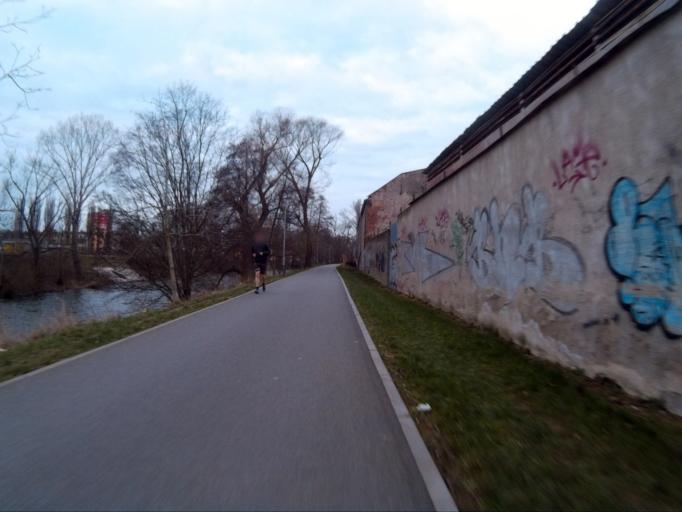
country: CZ
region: South Moravian
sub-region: Mesto Brno
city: Brno
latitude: 49.1778
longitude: 16.6152
